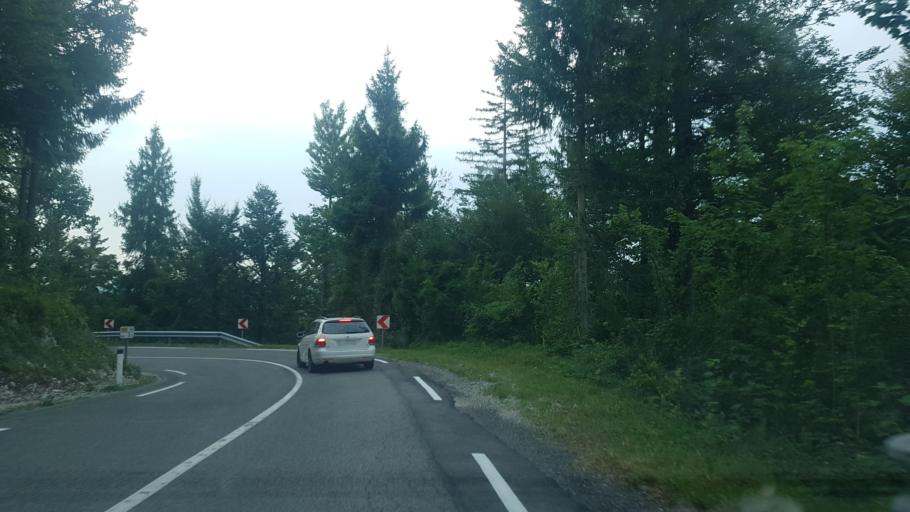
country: SI
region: Logatec
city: Logatec
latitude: 45.8902
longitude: 14.1570
